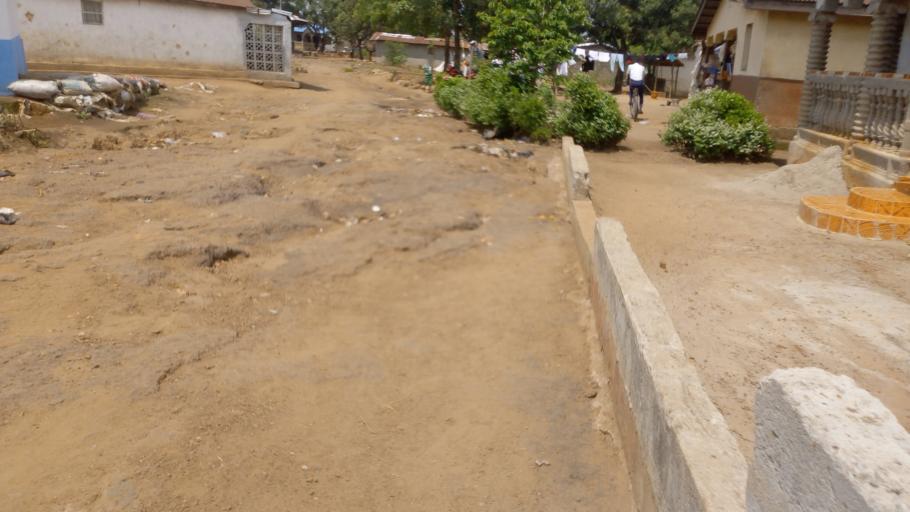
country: SL
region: Western Area
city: Waterloo
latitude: 8.3269
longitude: -13.0766
